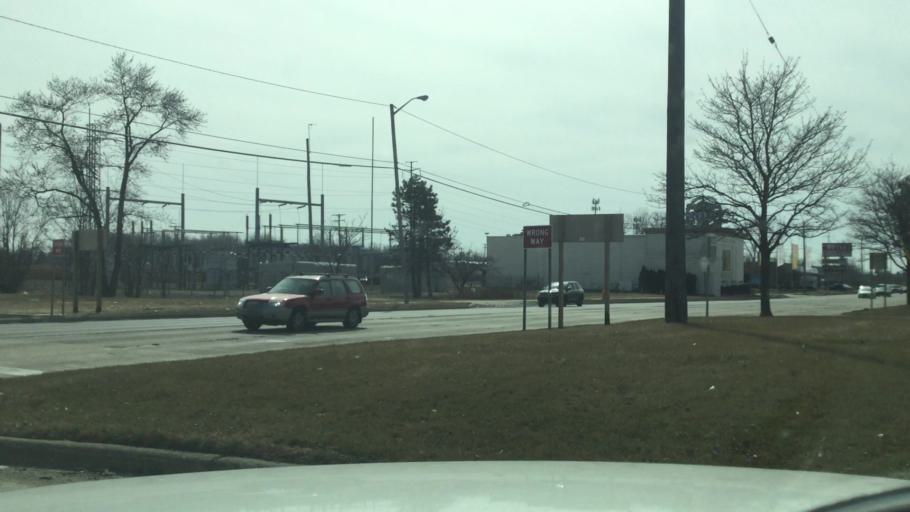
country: US
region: Michigan
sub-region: Wayne County
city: Inkster
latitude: 42.2891
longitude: -83.3310
